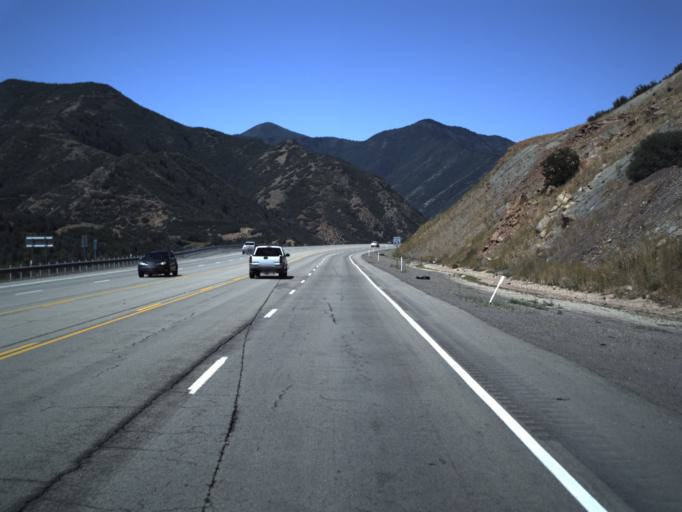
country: US
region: Utah
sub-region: Utah County
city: Mapleton
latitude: 40.0291
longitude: -111.5064
